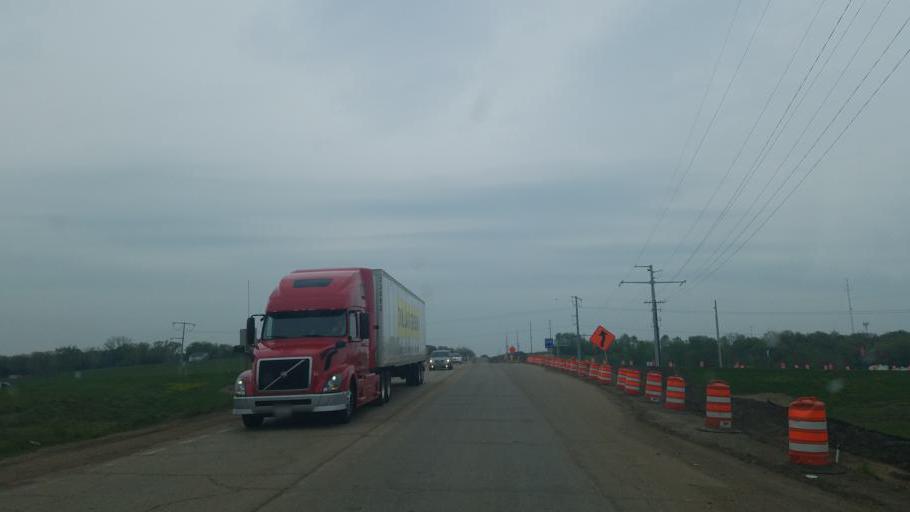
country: US
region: Wisconsin
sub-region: Dane County
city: Cottage Grove
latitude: 42.9994
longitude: -89.2003
